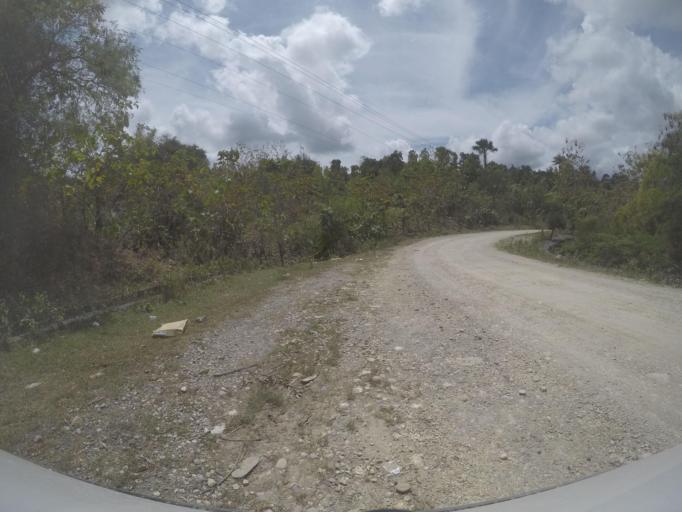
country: TL
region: Viqueque
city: Viqueque
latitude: -8.8851
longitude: 126.3855
